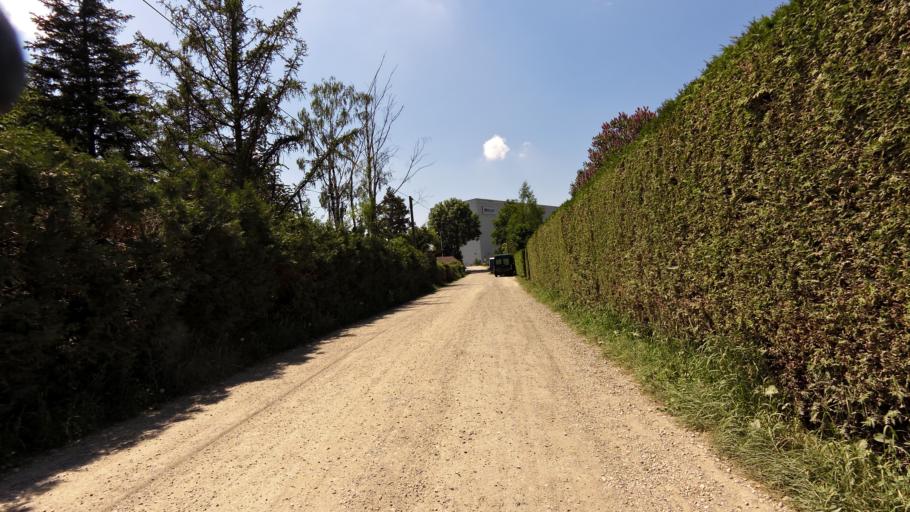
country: DE
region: Bavaria
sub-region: Lower Bavaria
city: Tiefenbach
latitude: 48.5449
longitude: 12.1001
